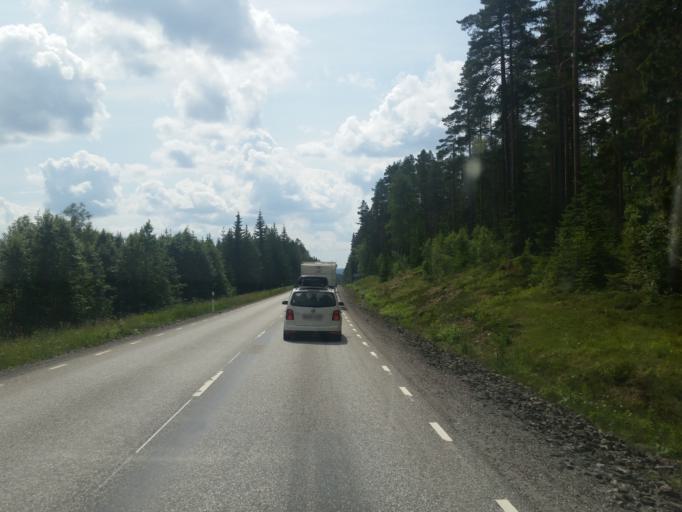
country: SE
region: OErebro
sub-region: Ljusnarsbergs Kommun
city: Kopparberg
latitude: 59.9122
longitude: 15.0224
